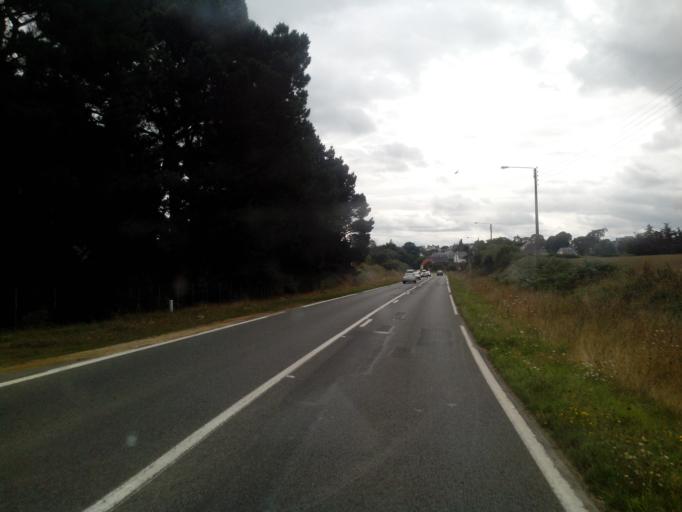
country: FR
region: Brittany
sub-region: Departement des Cotes-d'Armor
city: Etables-sur-Mer
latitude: 48.6308
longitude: -2.8235
